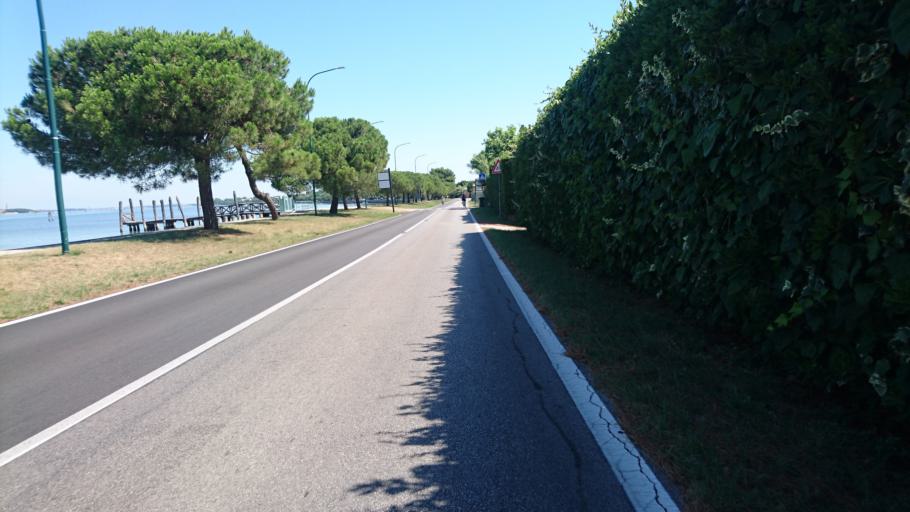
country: IT
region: Veneto
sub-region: Provincia di Venezia
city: San Pietro in Volta
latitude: 45.3580
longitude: 12.3293
